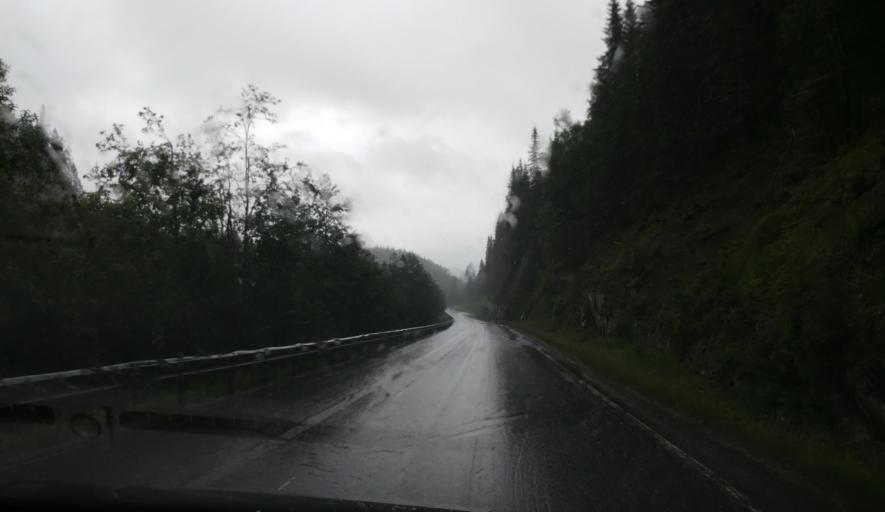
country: NO
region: Sor-Trondelag
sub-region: Selbu
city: Mebonden
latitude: 63.3185
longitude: 11.0840
